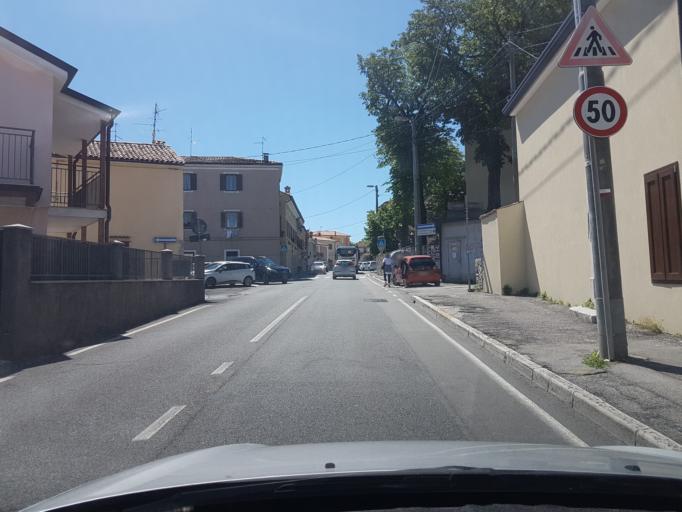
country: IT
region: Friuli Venezia Giulia
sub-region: Provincia di Trieste
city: Villa Opicina
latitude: 45.6903
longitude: 13.7873
